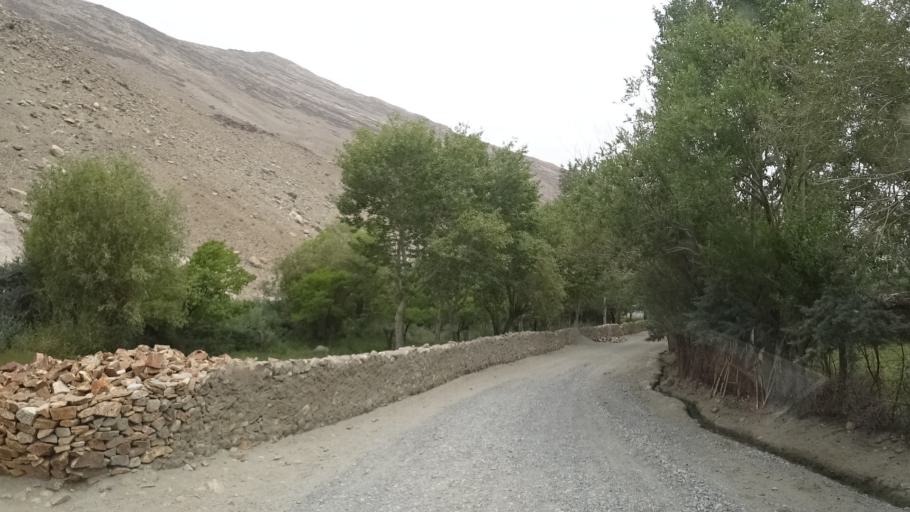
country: AF
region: Badakhshan
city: Khandud
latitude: 37.0217
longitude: 72.5850
